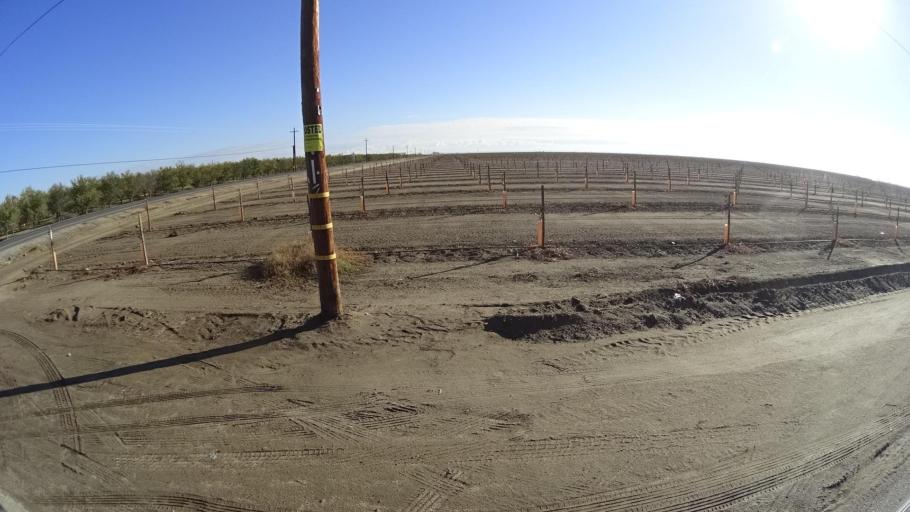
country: US
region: California
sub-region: Kern County
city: Delano
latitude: 35.7174
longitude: -119.3118
